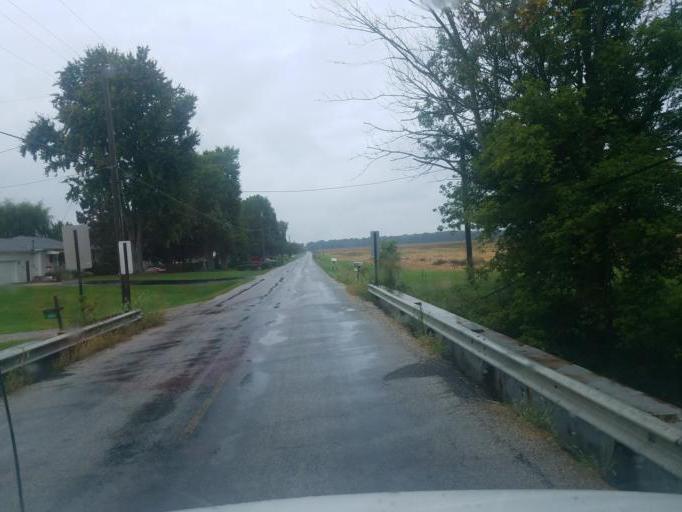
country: US
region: Ohio
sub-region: Medina County
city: Seville
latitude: 40.9823
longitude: -81.8585
